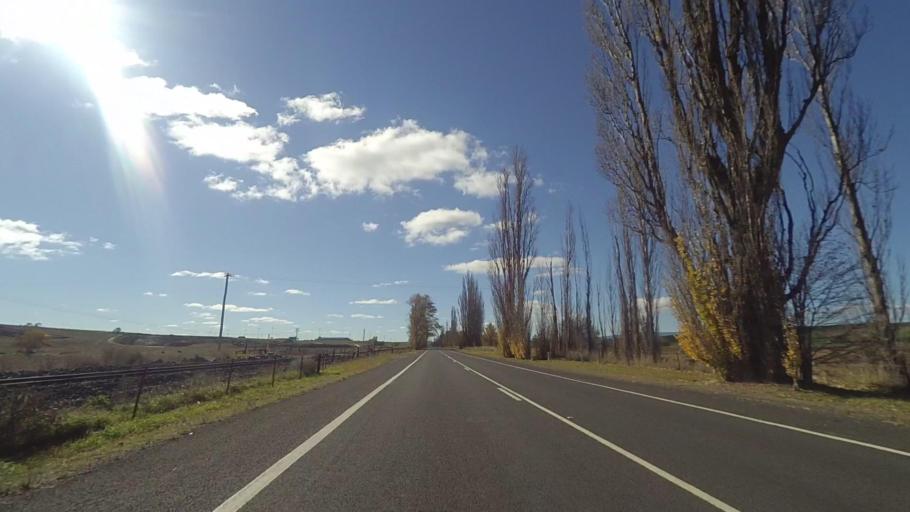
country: AU
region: New South Wales
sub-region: Bathurst Regional
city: Perthville
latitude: -33.4592
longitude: 149.5734
